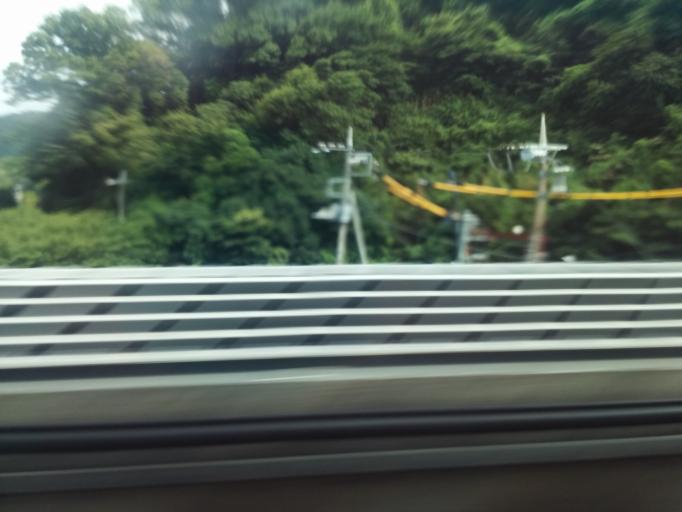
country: JP
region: Kanagawa
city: Yugawara
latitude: 35.1409
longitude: 139.0938
